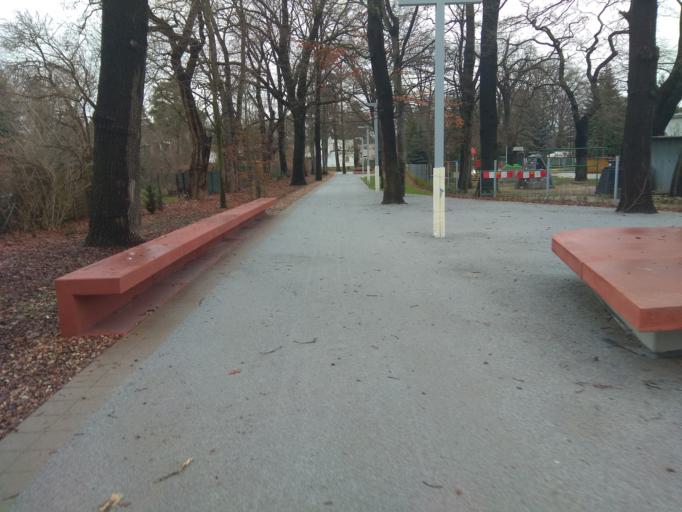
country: PL
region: Lower Silesian Voivodeship
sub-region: Powiat wroclawski
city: Wroclaw
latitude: 51.1057
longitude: 17.0843
